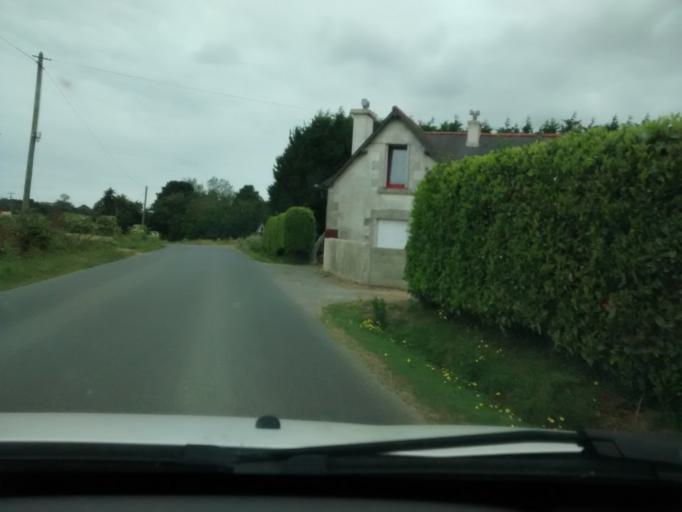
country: FR
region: Brittany
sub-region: Departement des Cotes-d'Armor
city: Trevou-Treguignec
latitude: 48.7889
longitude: -3.3361
